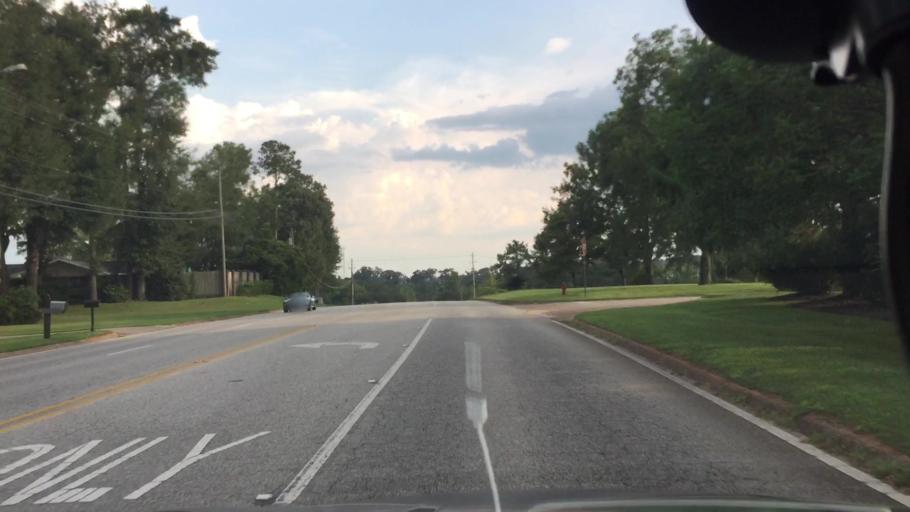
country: US
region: Alabama
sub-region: Coffee County
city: Enterprise
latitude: 31.3586
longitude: -85.8324
